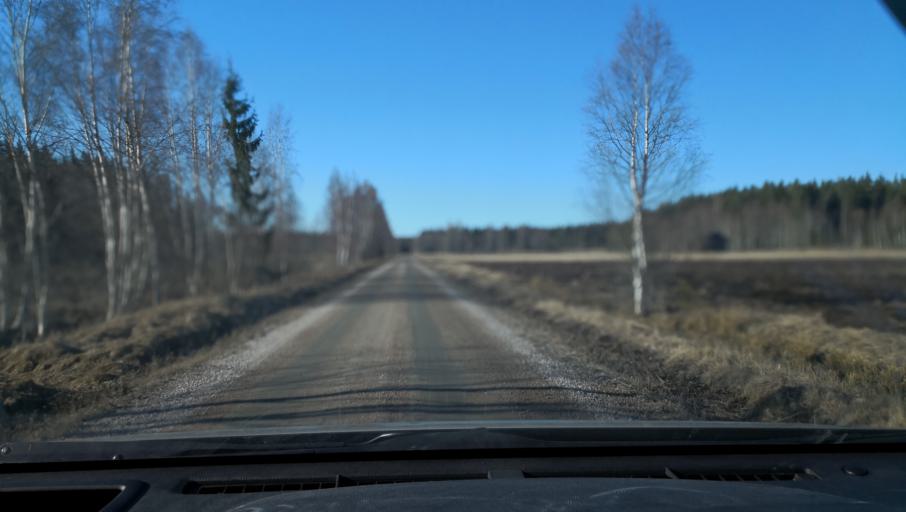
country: SE
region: Vaestmanland
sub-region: Sala Kommun
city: Sala
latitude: 60.1284
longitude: 16.6539
